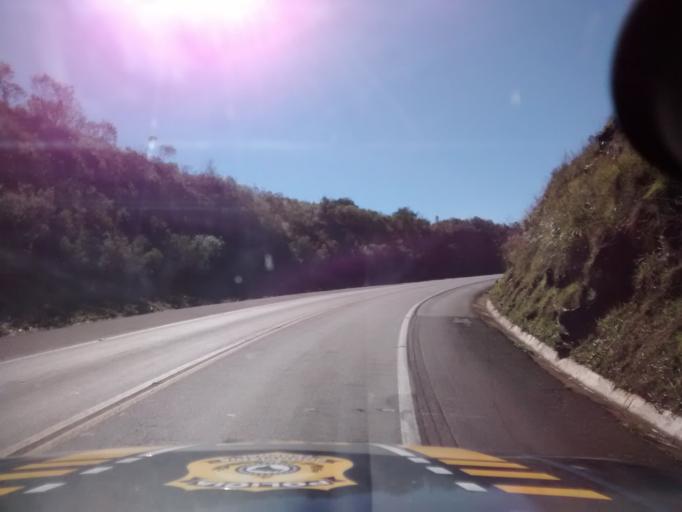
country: BR
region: Rio Grande do Sul
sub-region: Vacaria
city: Vacaria
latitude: -28.3405
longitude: -51.1533
